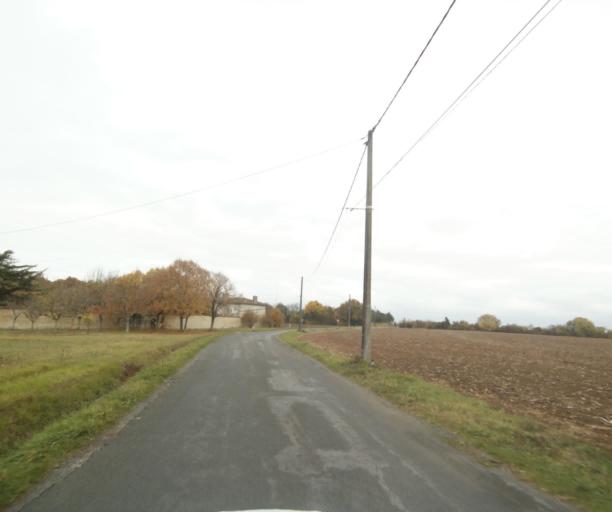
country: FR
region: Poitou-Charentes
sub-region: Departement de la Charente-Maritime
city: Saintes
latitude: 45.7416
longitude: -0.6739
